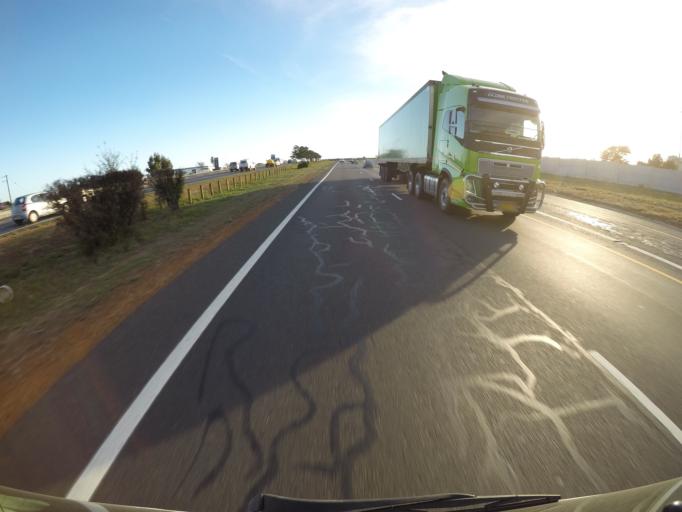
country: ZA
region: Western Cape
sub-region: City of Cape Town
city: Kraaifontein
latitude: -33.8553
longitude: 18.6995
